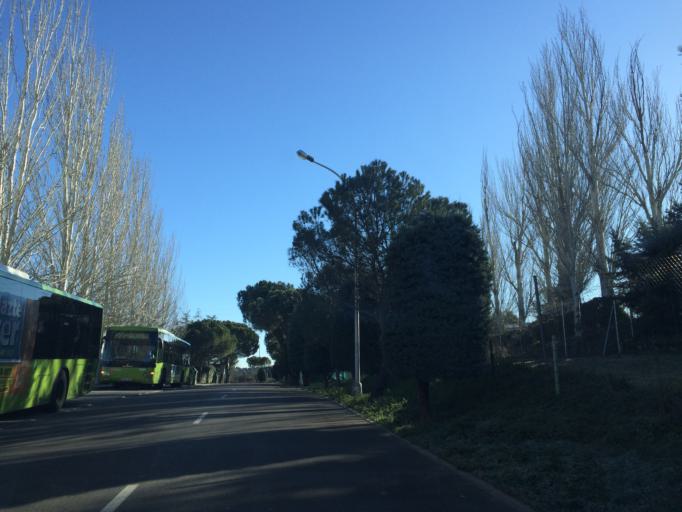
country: ES
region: Madrid
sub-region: Provincia de Madrid
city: Tres Cantos
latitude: 40.6116
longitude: -3.6821
